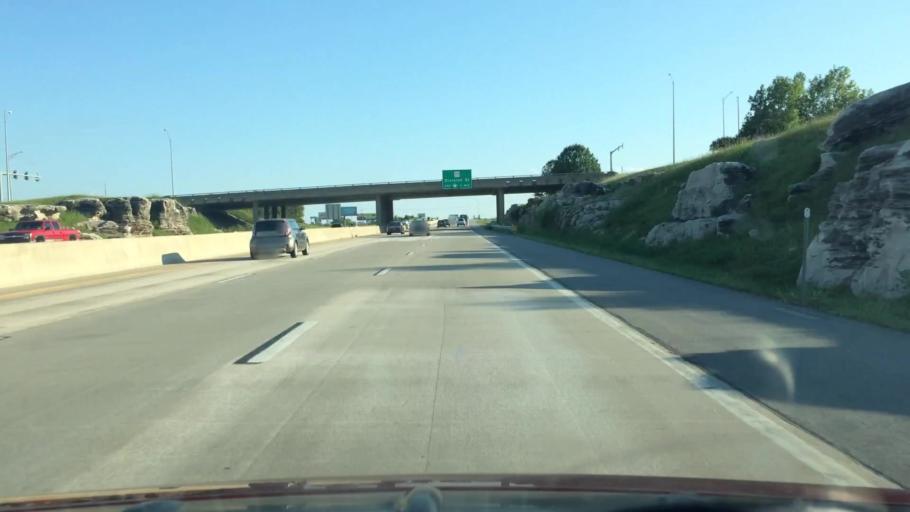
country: US
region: Missouri
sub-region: Greene County
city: Springfield
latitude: 37.2402
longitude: -93.2249
